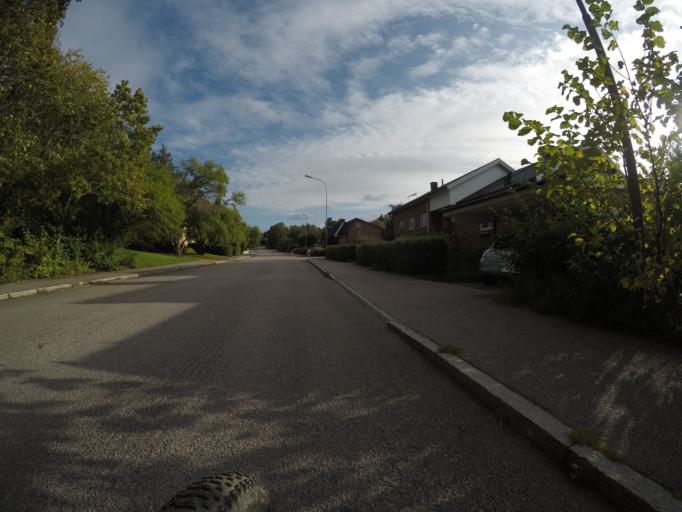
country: SE
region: Vaestmanland
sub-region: Kopings Kommun
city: Koping
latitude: 59.5140
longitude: 16.0115
